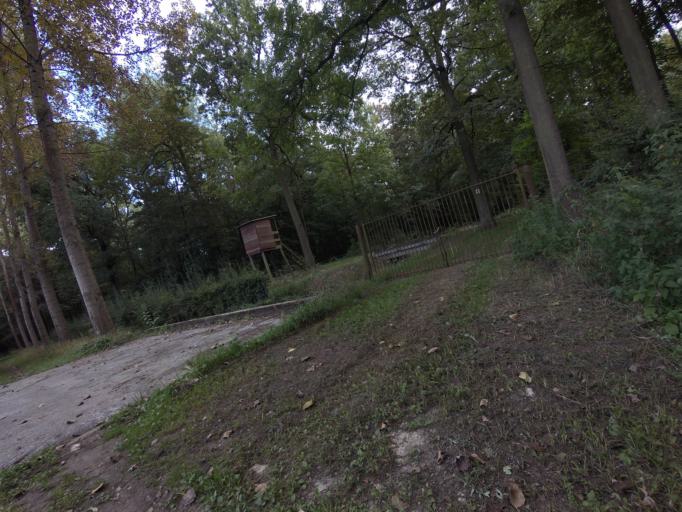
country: BE
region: Flanders
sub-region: Provincie Vlaams-Brabant
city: Steenokkerzeel
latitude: 50.9346
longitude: 4.5123
